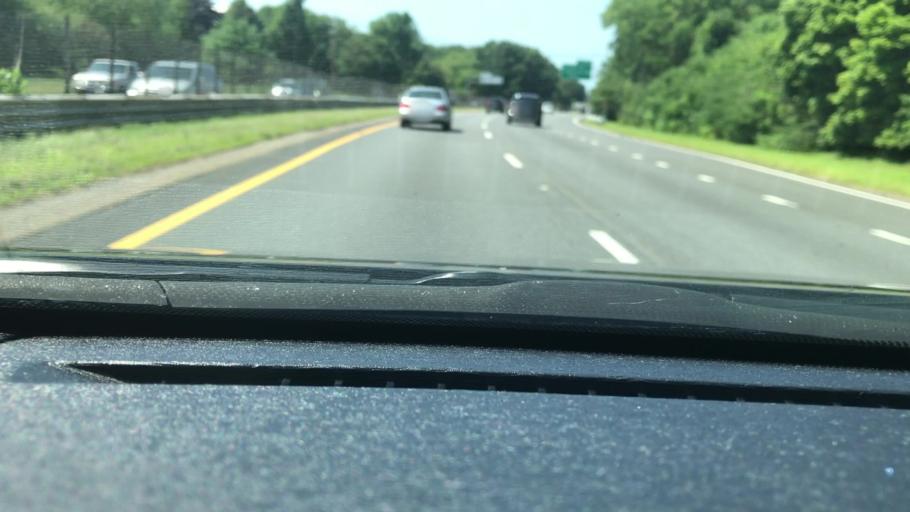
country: US
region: Massachusetts
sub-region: Essex County
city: Danvers
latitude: 42.5715
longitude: -70.9090
